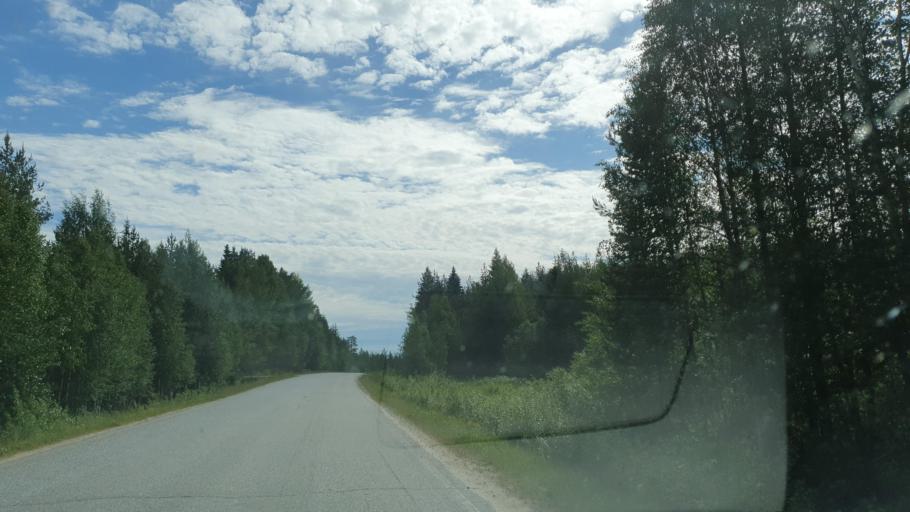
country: FI
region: Kainuu
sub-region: Kehys-Kainuu
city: Kuhmo
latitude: 64.4614
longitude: 29.5350
